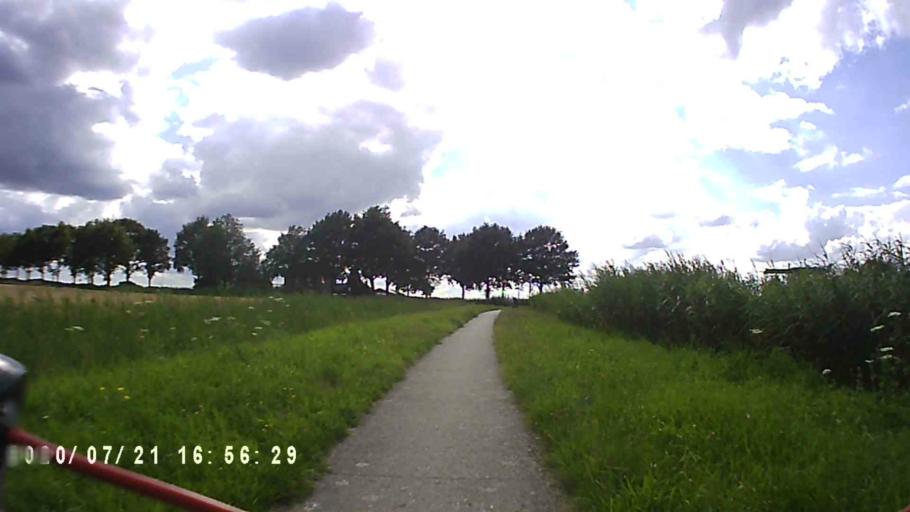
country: NL
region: Groningen
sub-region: Gemeente Hoogezand-Sappemeer
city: Hoogezand
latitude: 53.1289
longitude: 6.7601
